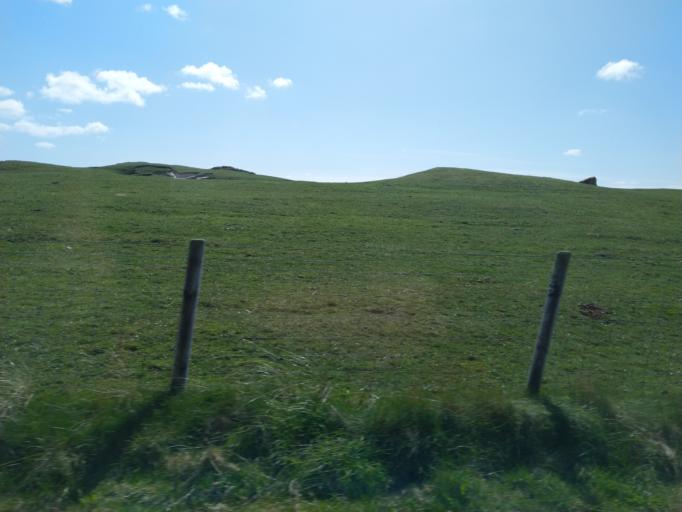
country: GB
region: Scotland
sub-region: Eilean Siar
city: Barra
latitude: 56.4842
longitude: -6.8916
